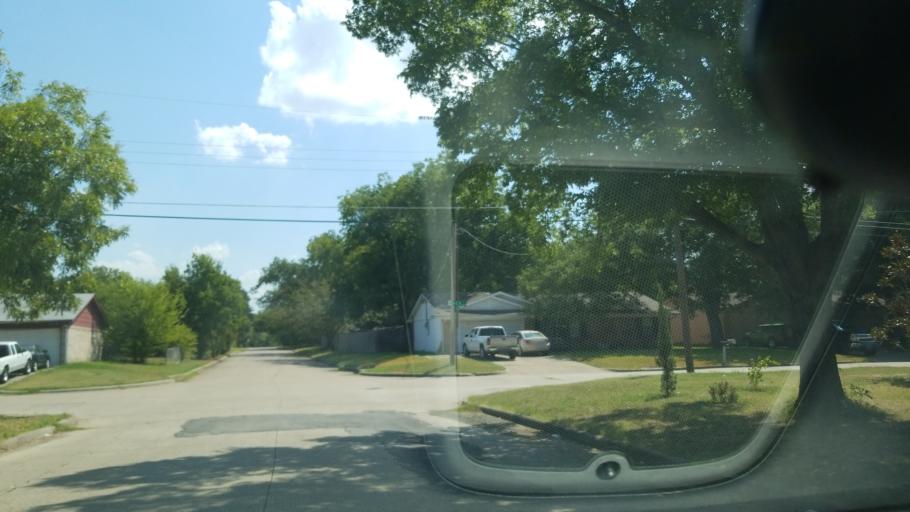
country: US
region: Texas
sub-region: Dallas County
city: Grand Prairie
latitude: 32.7137
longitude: -96.9835
